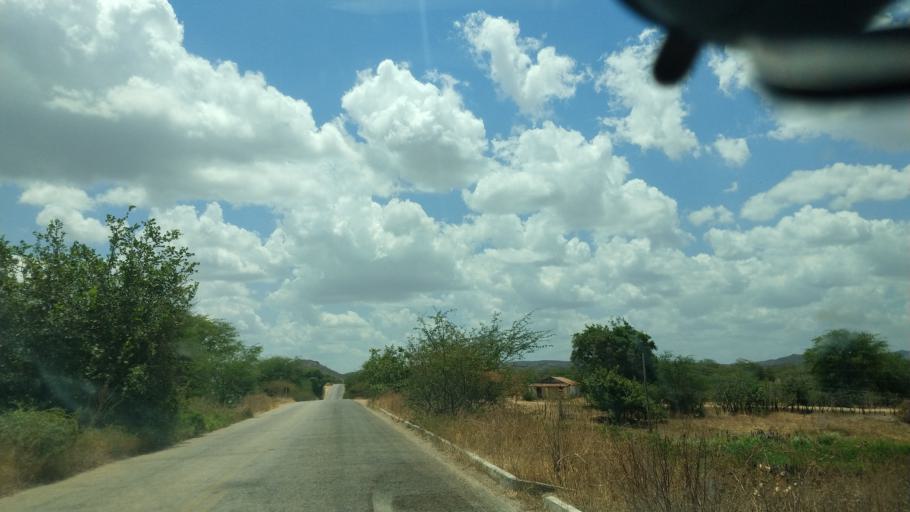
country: BR
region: Rio Grande do Norte
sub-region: Currais Novos
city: Currais Novos
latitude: -6.2748
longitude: -36.5418
